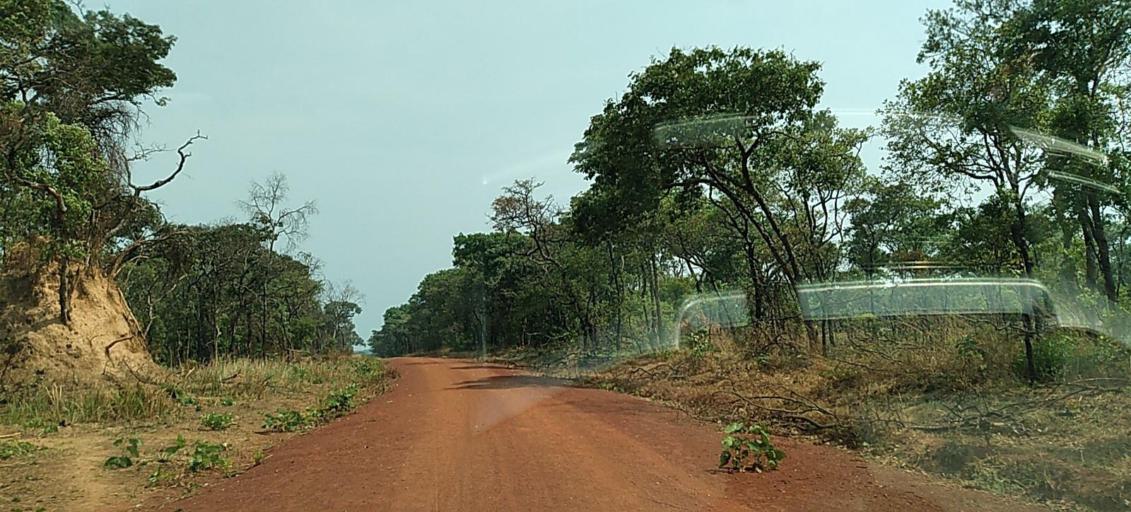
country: ZM
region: North-Western
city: Kansanshi
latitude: -12.0080
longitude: 26.8448
